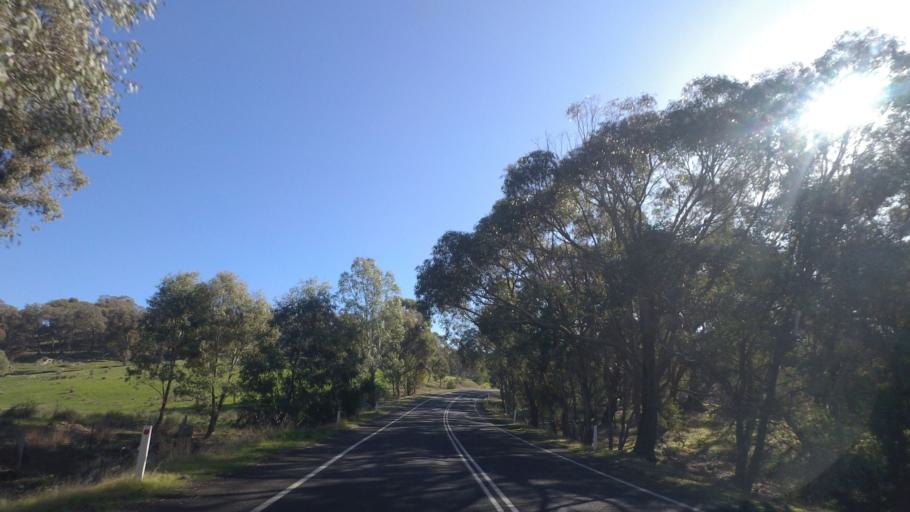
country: AU
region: Victoria
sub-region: Greater Bendigo
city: Kennington
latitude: -36.9181
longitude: 144.3362
